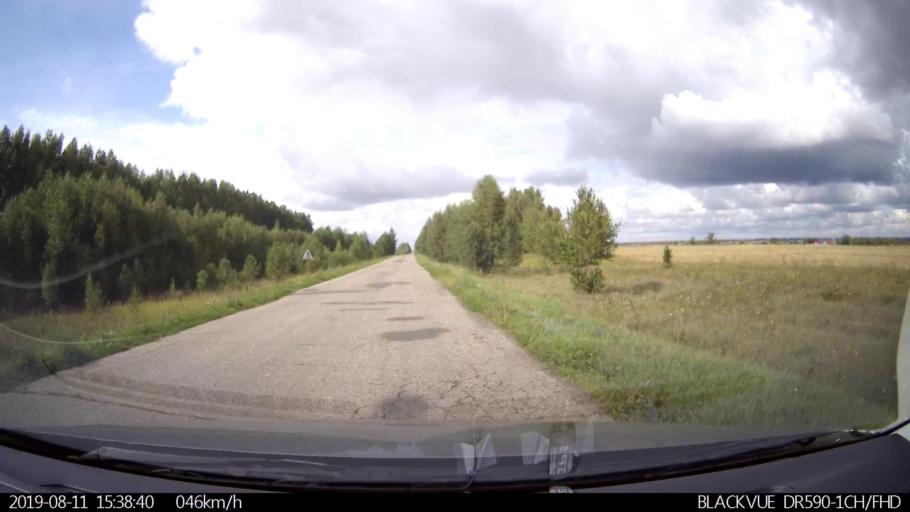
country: RU
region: Ulyanovsk
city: Ignatovka
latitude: 53.8629
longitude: 47.6405
